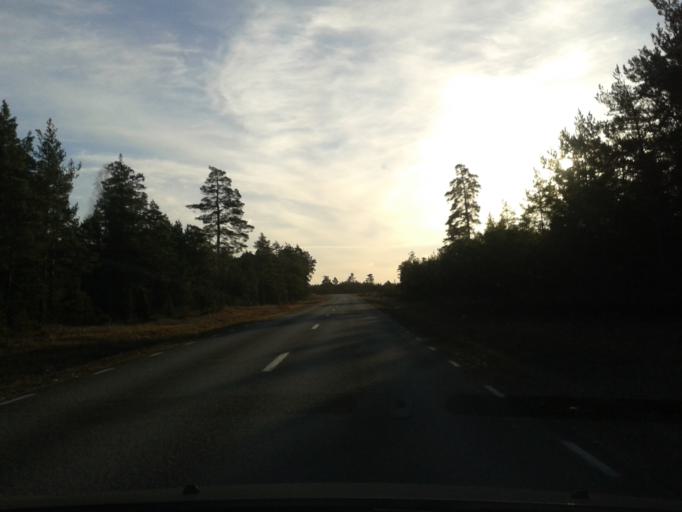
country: SE
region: Gotland
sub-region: Gotland
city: Hemse
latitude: 57.4028
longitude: 18.6378
